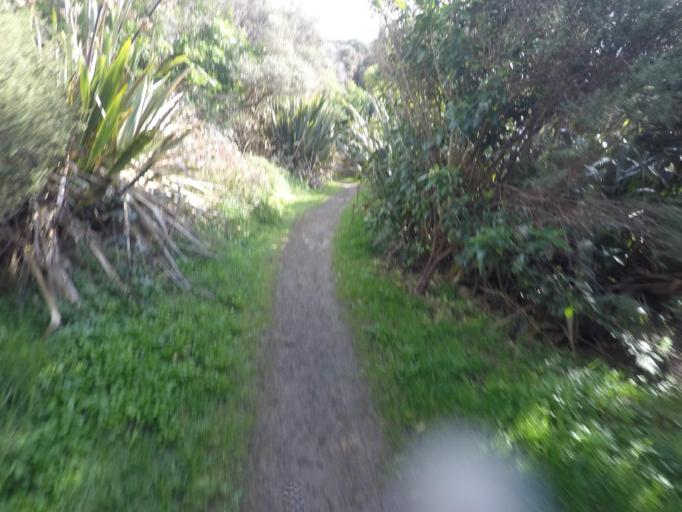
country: NZ
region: Auckland
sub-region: Auckland
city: Manukau City
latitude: -36.9975
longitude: 174.9102
